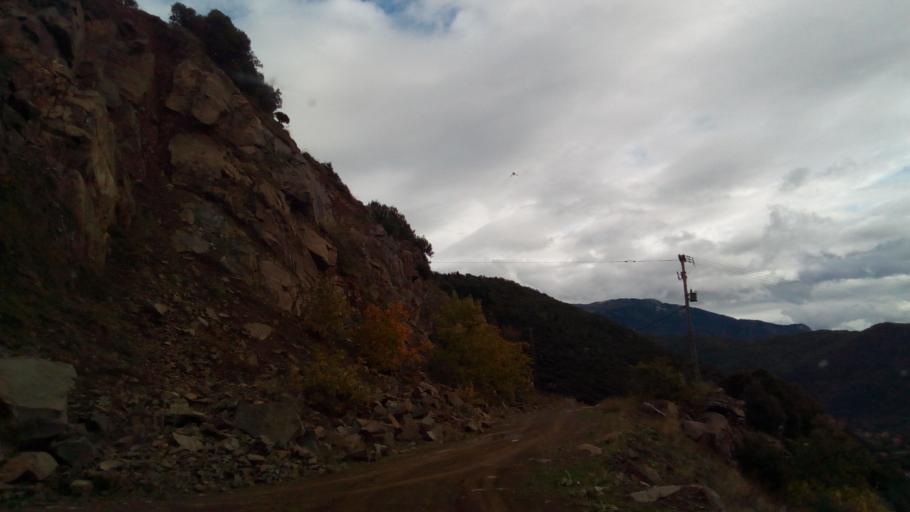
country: GR
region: West Greece
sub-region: Nomos Aitolias kai Akarnanias
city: Nafpaktos
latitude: 38.5641
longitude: 21.9590
